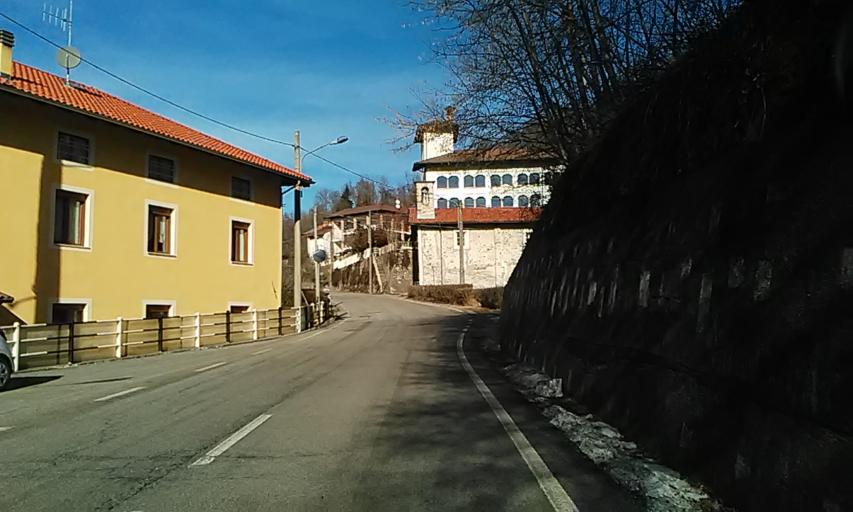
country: IT
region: Piedmont
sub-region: Provincia di Vercelli
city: Cellio
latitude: 45.7328
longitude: 8.3003
